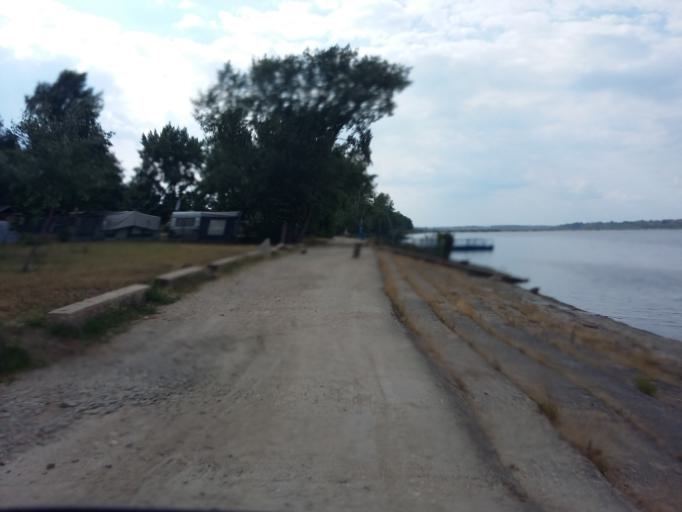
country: CZ
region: South Moravian
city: Sakvice
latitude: 48.8870
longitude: 16.6566
